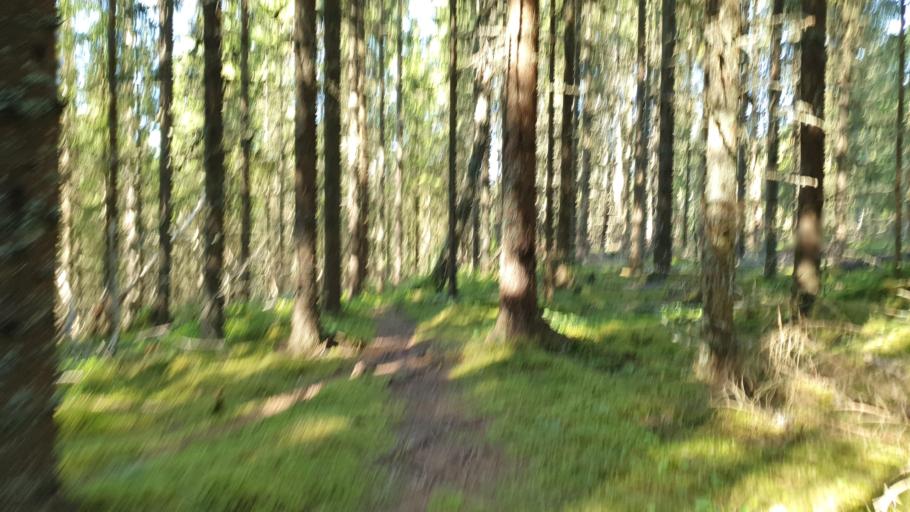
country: NO
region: Nord-Trondelag
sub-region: Levanger
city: Levanger
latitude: 63.6901
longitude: 11.2642
